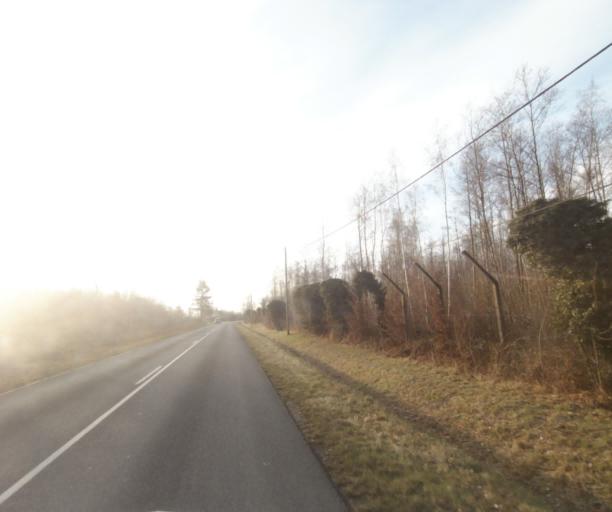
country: FR
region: Champagne-Ardenne
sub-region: Departement de la Haute-Marne
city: Chancenay
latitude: 48.6940
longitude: 4.9456
